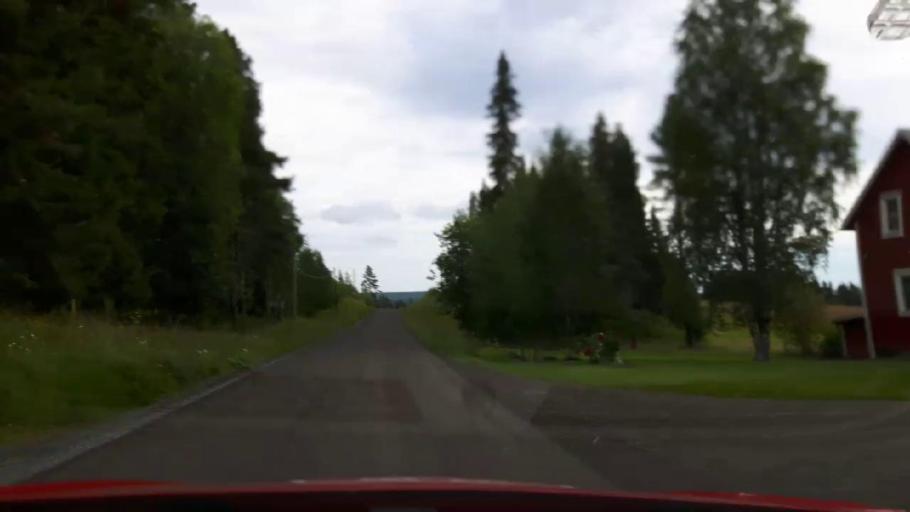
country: SE
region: Jaemtland
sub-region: OEstersunds Kommun
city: Lit
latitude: 63.4482
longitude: 15.2727
